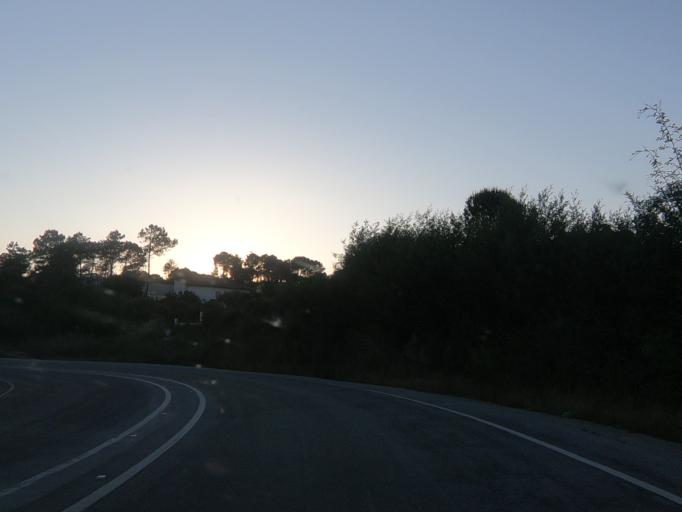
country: PT
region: Viseu
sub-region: Viseu
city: Abraveses
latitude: 40.6947
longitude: -7.9299
